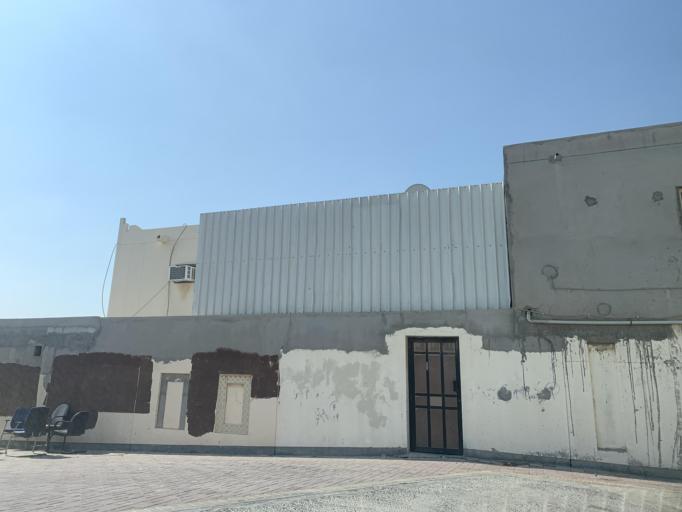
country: BH
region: Central Governorate
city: Madinat Hamad
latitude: 26.1109
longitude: 50.5011
